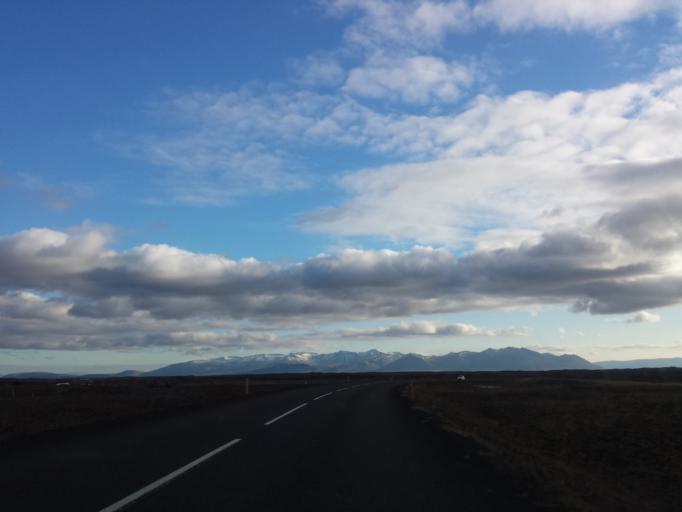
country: IS
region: West
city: Borgarnes
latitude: 64.6758
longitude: -22.0724
